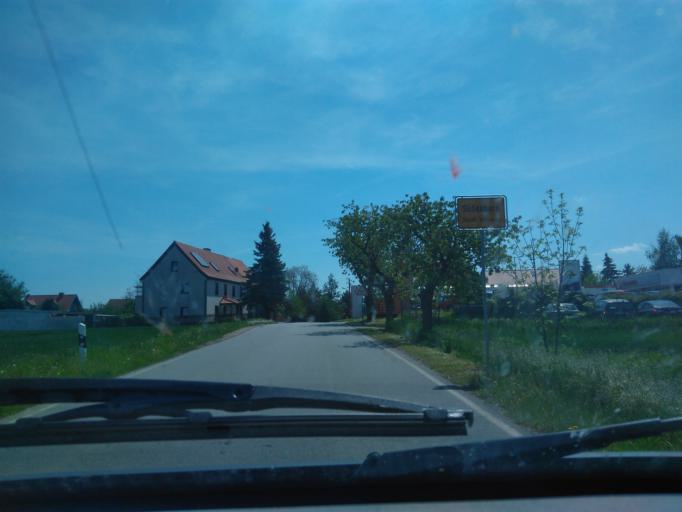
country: DE
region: Thuringia
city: Kromsdorf
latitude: 50.9863
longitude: 11.3882
